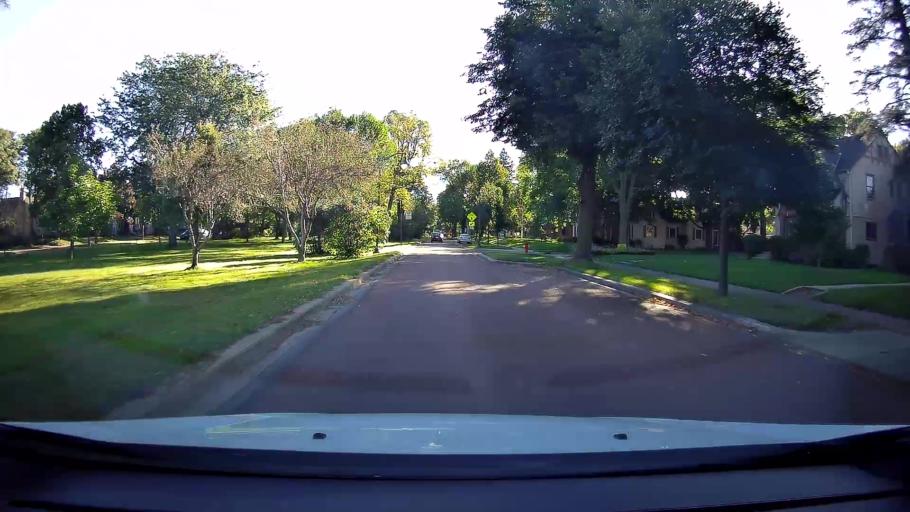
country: US
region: Minnesota
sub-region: Hennepin County
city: Richfield
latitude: 44.9161
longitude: -93.2263
